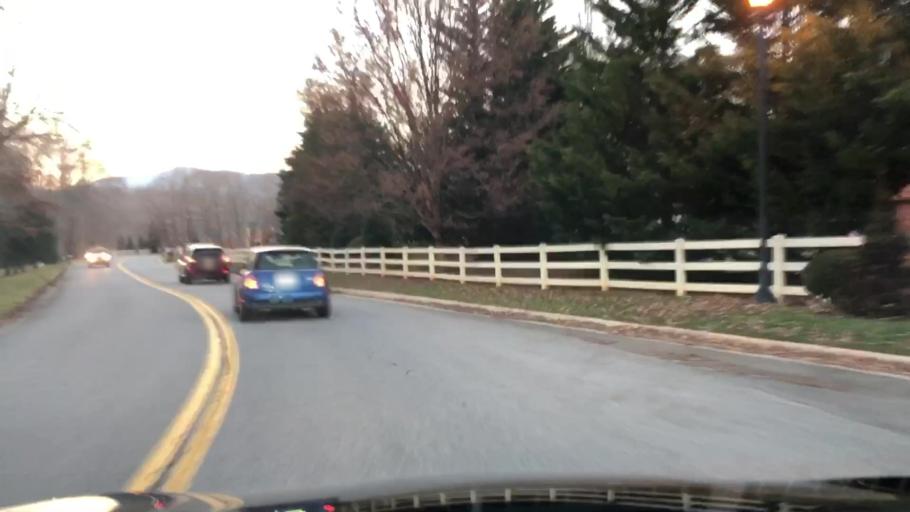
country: US
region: Virginia
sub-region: Bedford County
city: Forest
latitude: 37.4314
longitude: -79.2523
